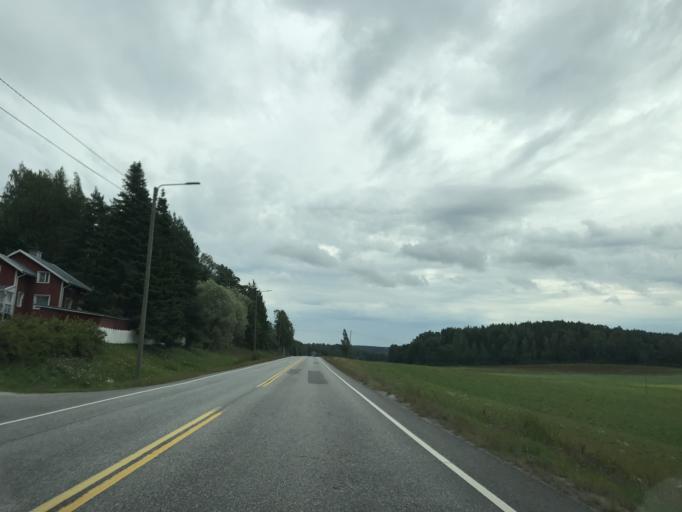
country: FI
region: Varsinais-Suomi
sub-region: Turku
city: Paimio
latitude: 60.4284
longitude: 22.6175
